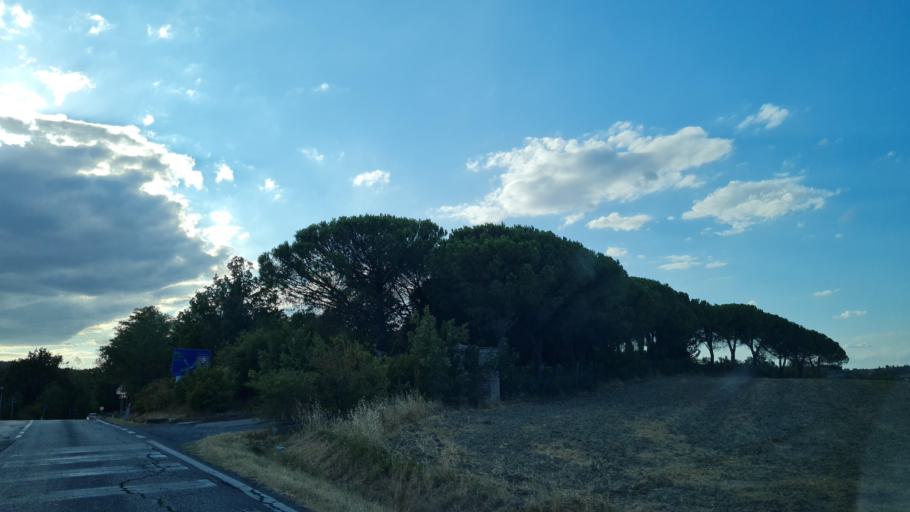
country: IT
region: Tuscany
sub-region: Provincia di Siena
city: Chianciano Terme
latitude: 43.0354
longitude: 11.8379
